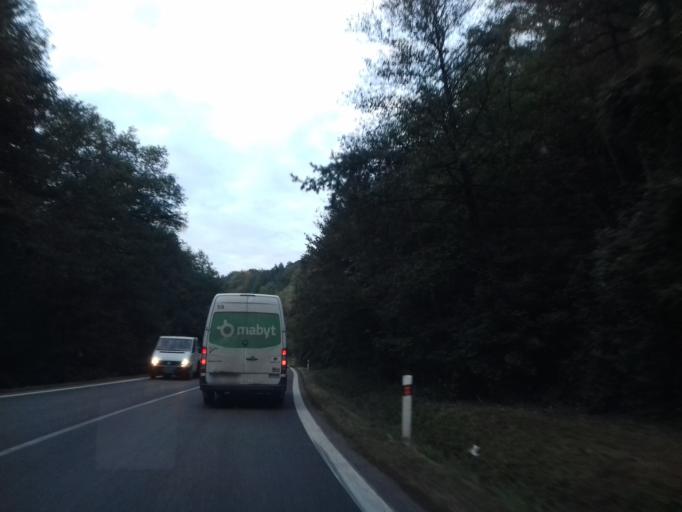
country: SK
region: Trenciansky
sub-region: Okres Trencin
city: Trencin
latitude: 48.9286
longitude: 17.9413
